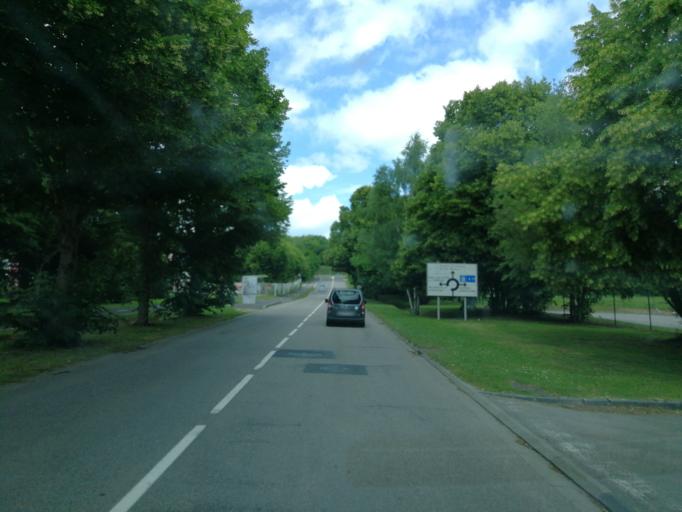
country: FR
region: Haute-Normandie
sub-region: Departement de l'Eure
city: Le Vaudreuil
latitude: 49.2516
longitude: 1.1788
